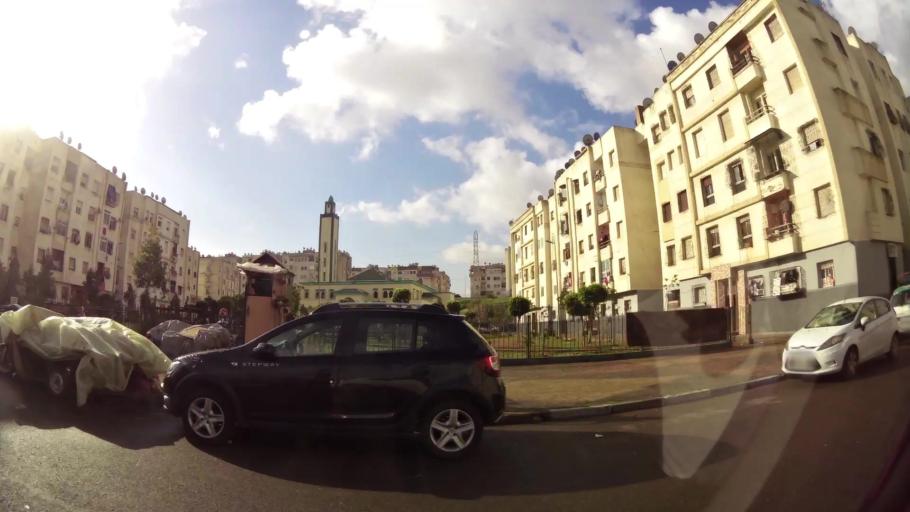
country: MA
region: Grand Casablanca
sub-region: Mediouna
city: Tit Mellil
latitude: 33.5940
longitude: -7.5381
